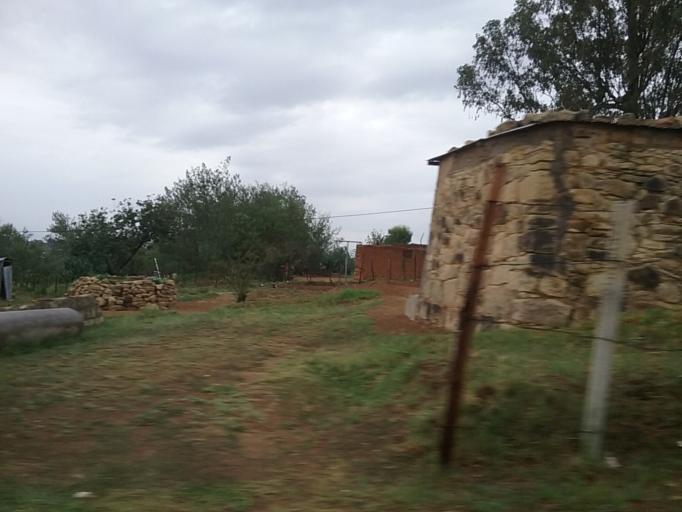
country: LS
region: Berea
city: Teyateyaneng
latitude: -29.1354
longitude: 27.7348
